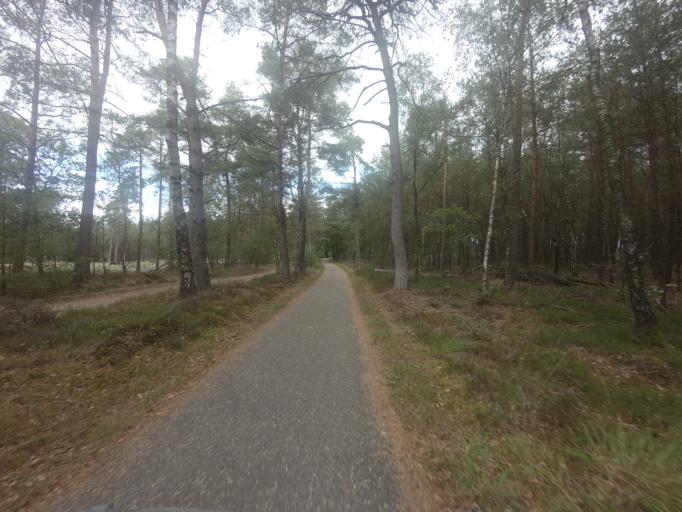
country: NL
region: Friesland
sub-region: Gemeente Weststellingwerf
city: Noordwolde
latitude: 52.9030
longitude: 6.2415
